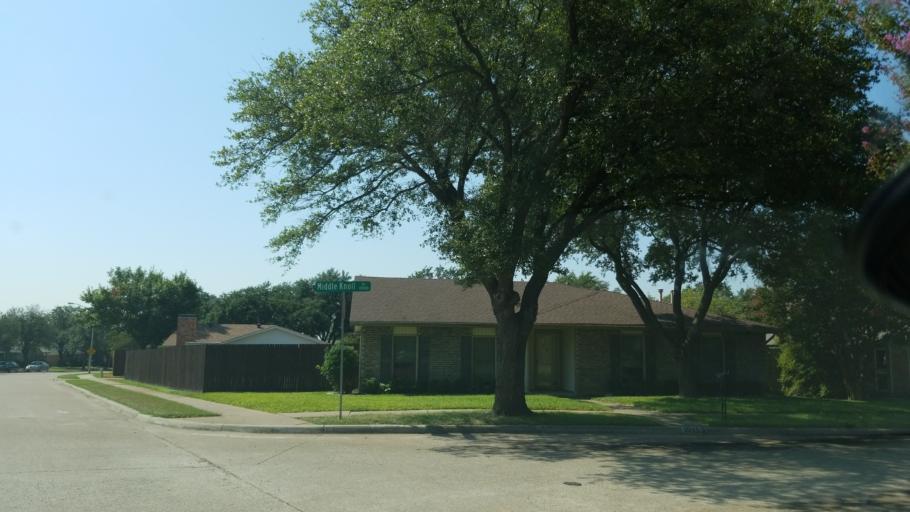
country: US
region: Texas
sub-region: Dallas County
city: Garland
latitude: 32.8759
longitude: -96.6942
